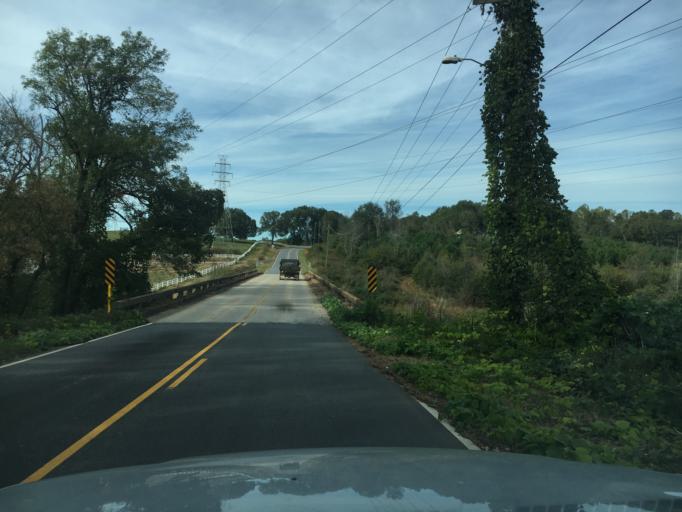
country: US
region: South Carolina
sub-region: Spartanburg County
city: Duncan
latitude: 34.9255
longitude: -82.1445
